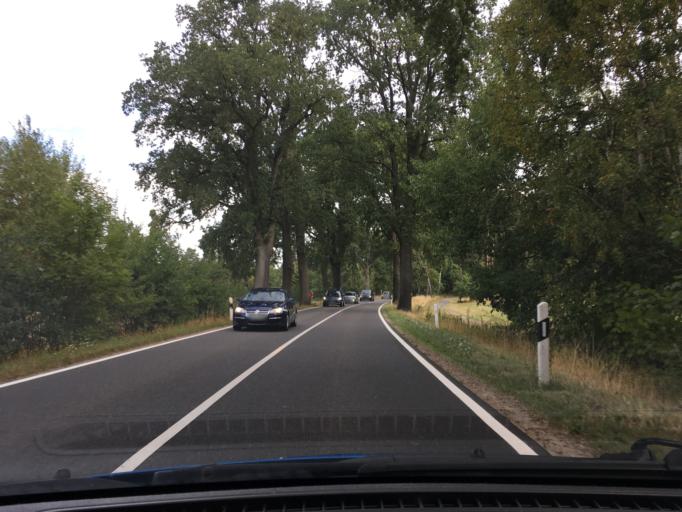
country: DE
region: Mecklenburg-Vorpommern
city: Malliss
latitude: 53.2032
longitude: 11.3032
